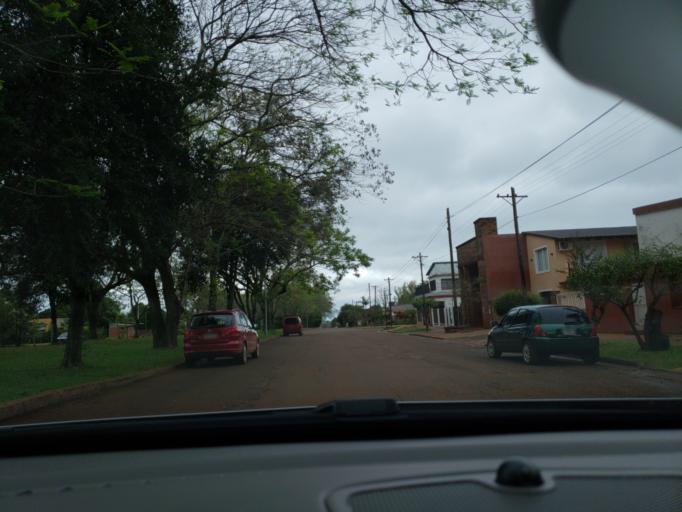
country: AR
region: Misiones
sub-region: Departamento de Apostoles
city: Apostoles
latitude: -27.9209
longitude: -55.7627
